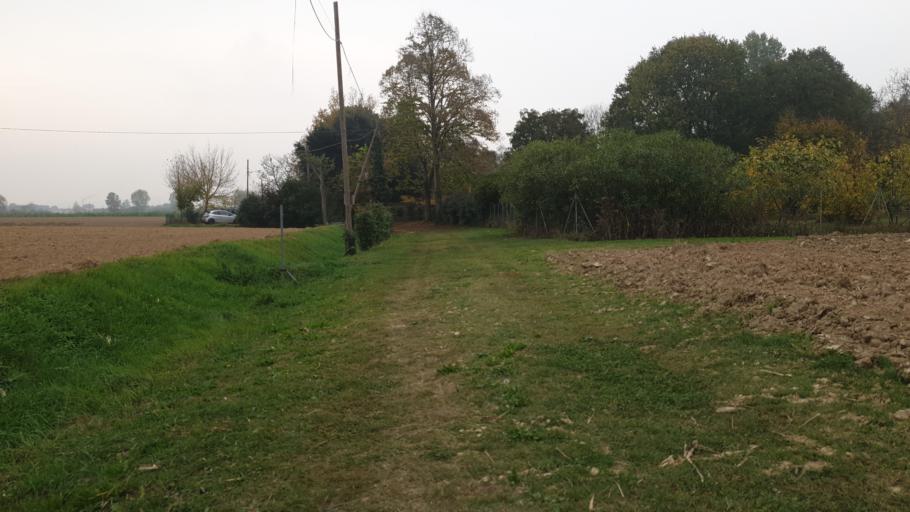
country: IT
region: Veneto
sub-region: Provincia di Padova
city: Bertipaglia
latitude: 45.3196
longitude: 11.8957
